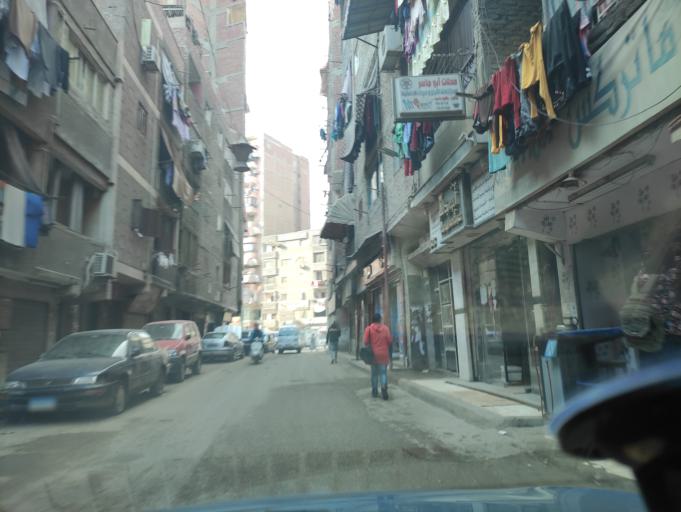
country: EG
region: Muhafazat al Qahirah
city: Cairo
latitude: 30.1245
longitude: 31.3041
